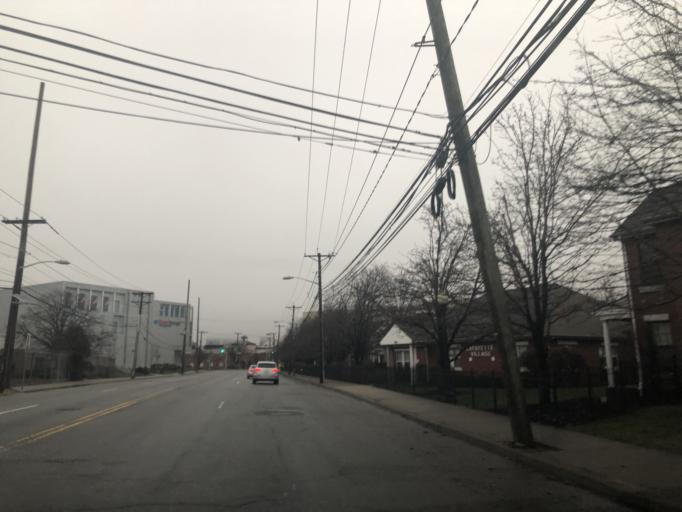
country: US
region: New Jersey
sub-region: Hudson County
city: Jersey City
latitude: 40.7172
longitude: -74.0611
